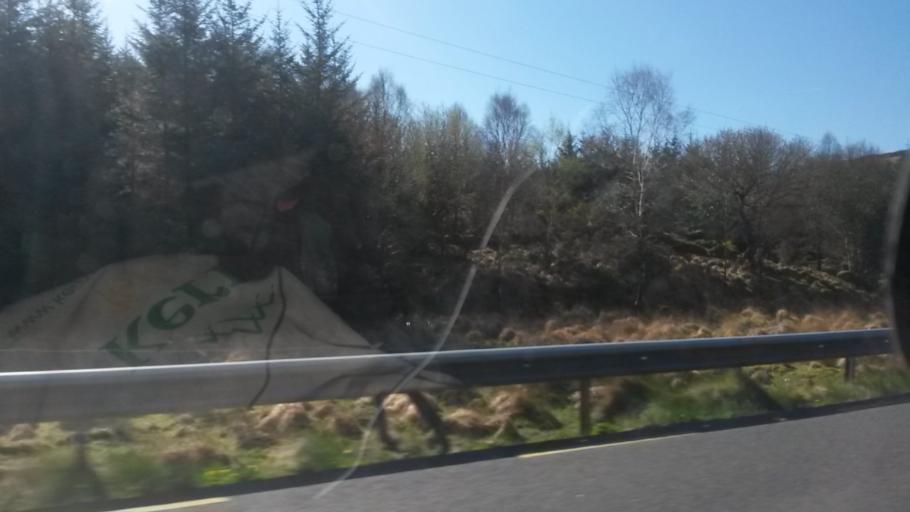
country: IE
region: Munster
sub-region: Ciarrai
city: Cill Airne
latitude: 51.9711
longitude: -9.3471
